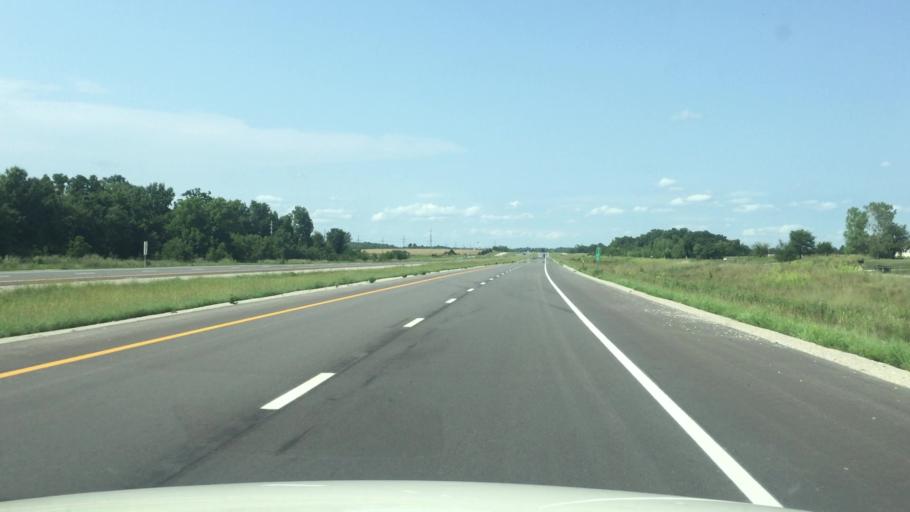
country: US
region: Kansas
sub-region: Linn County
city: La Cygne
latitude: 38.3101
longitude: -94.6775
